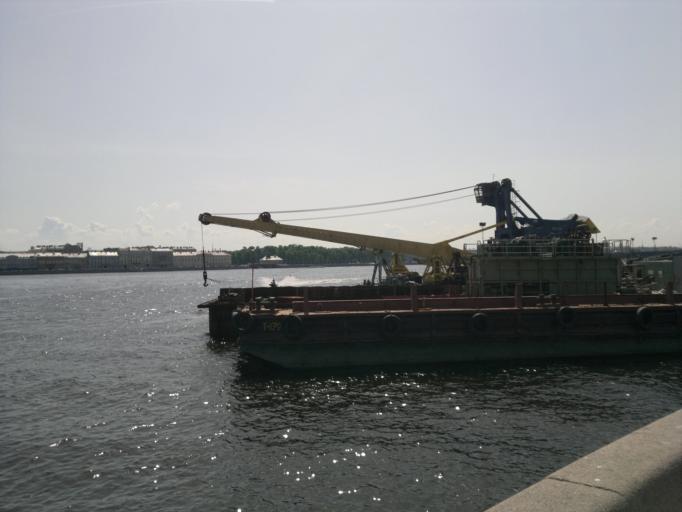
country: RU
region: St.-Petersburg
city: Saint Petersburg
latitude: 59.9540
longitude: 30.3377
